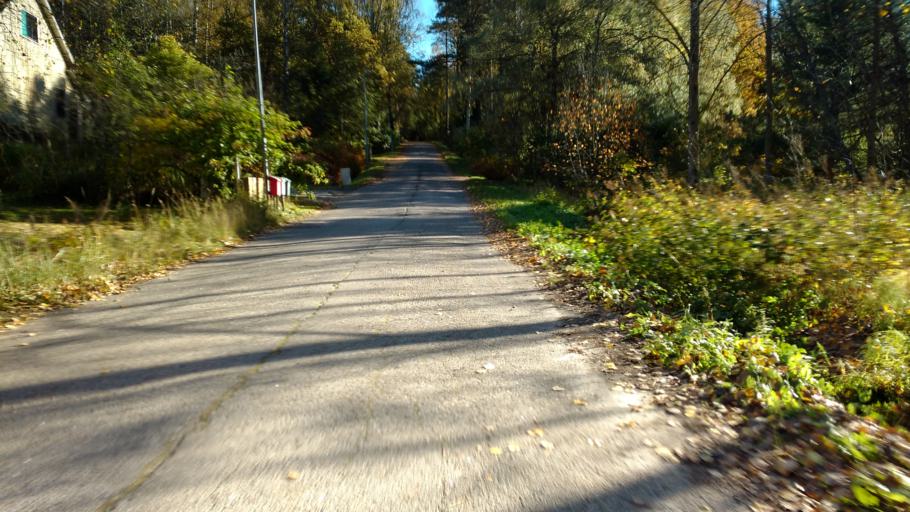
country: FI
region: Varsinais-Suomi
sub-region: Salo
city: Salo
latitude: 60.3974
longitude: 23.1694
